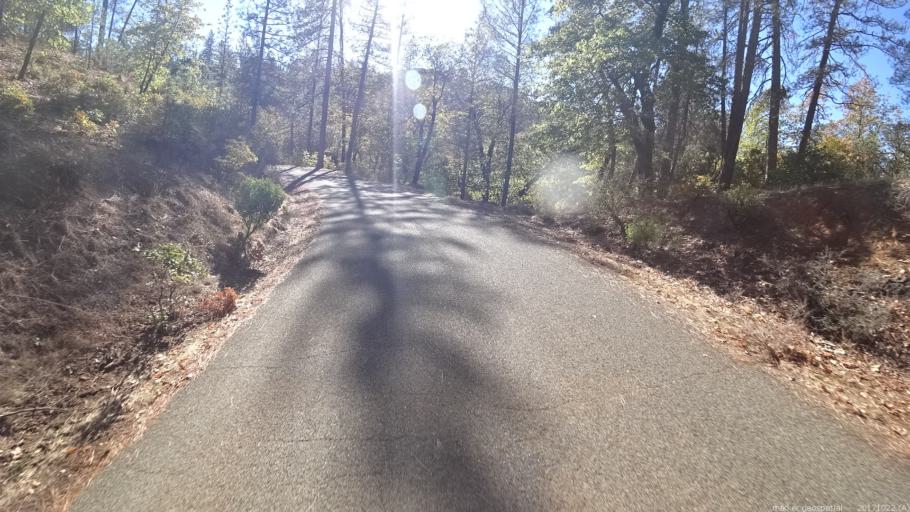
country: US
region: California
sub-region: Shasta County
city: Shasta Lake
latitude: 40.8787
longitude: -122.3671
